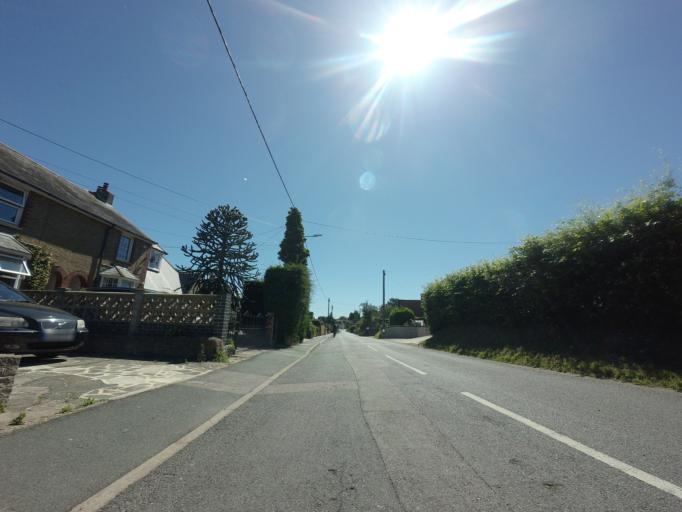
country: GB
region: England
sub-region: Kent
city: Ash
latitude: 51.2766
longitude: 1.2886
